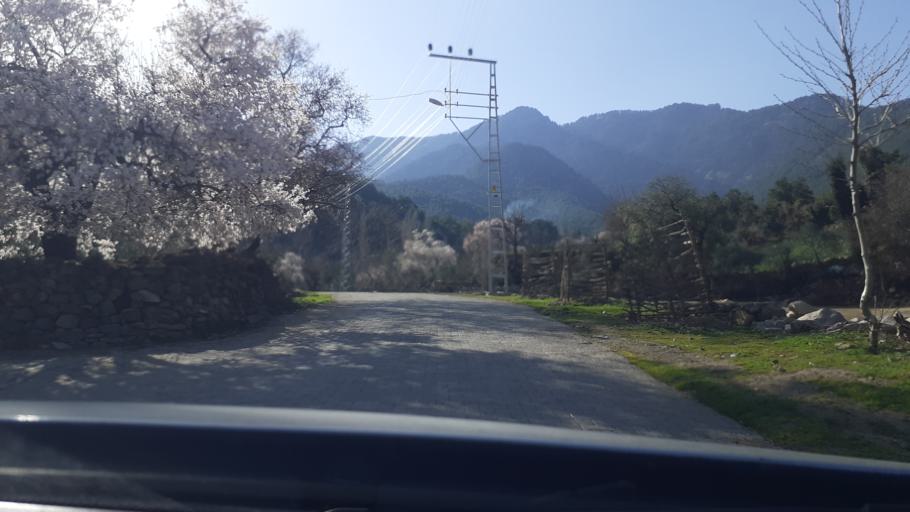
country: TR
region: Hatay
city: Aktepe
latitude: 36.7584
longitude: 36.4473
